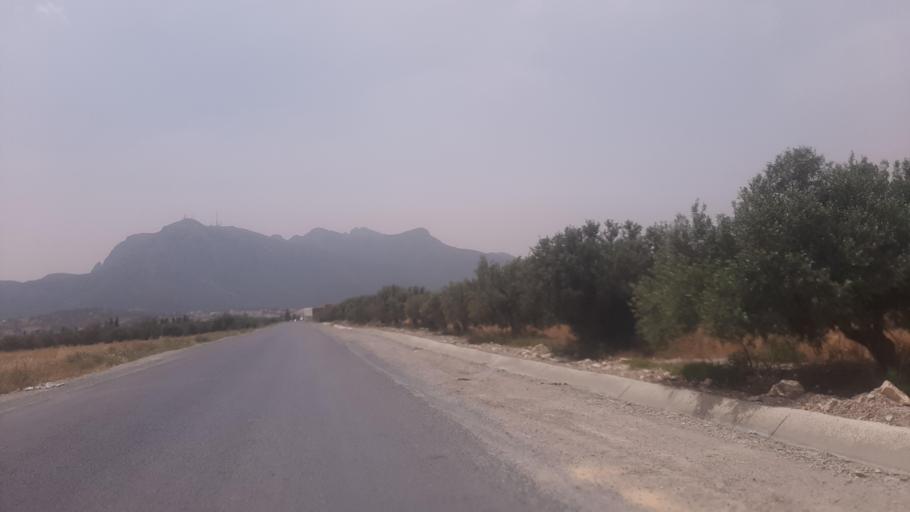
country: TN
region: Zaghwan
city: Zaghouan
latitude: 36.4216
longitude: 10.1374
